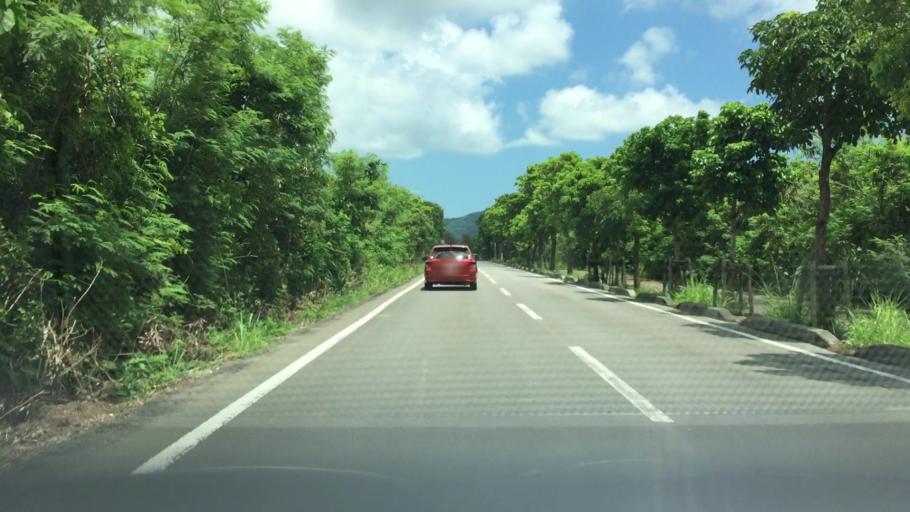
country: JP
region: Okinawa
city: Ishigaki
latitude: 24.3973
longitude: 124.1411
